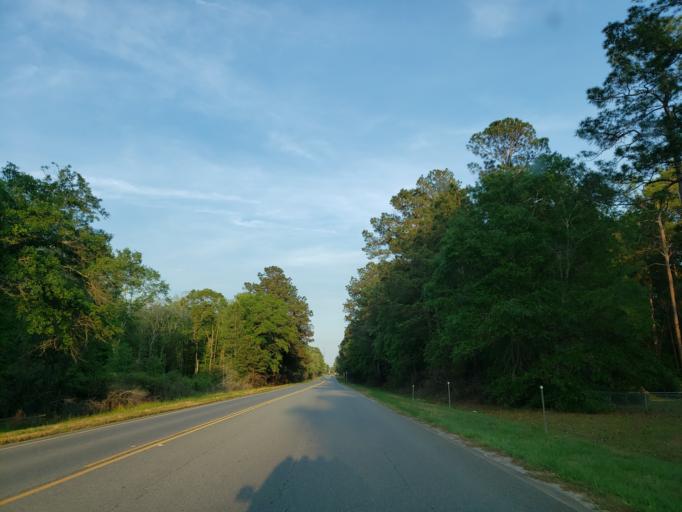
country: US
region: Georgia
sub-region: Lowndes County
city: Hahira
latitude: 30.9950
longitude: -83.4097
